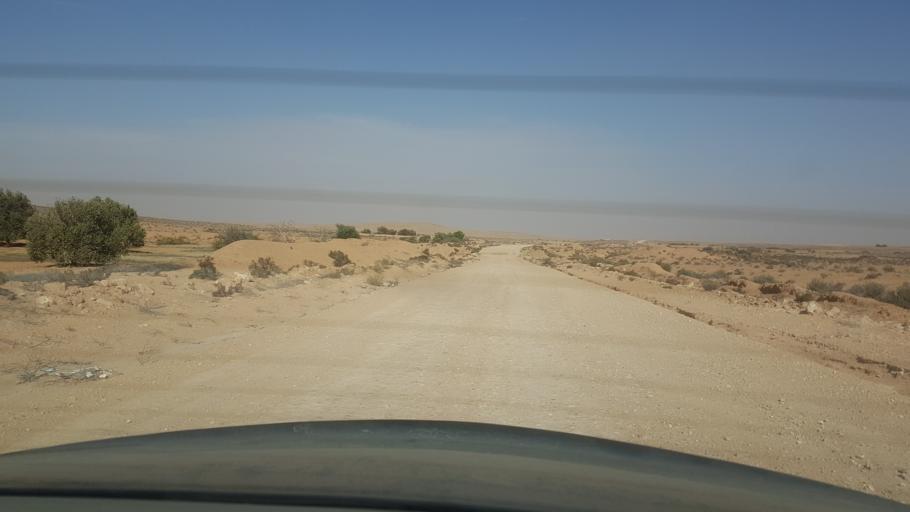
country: TN
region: Qabis
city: El Hamma
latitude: 33.6620
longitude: 9.7350
